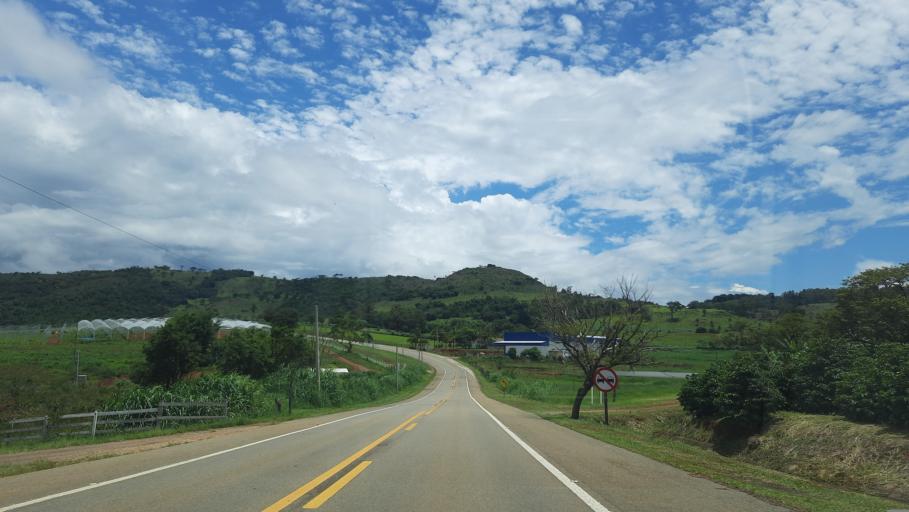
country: BR
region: Sao Paulo
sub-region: Vargem Grande Do Sul
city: Vargem Grande do Sul
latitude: -21.8193
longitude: -46.7840
